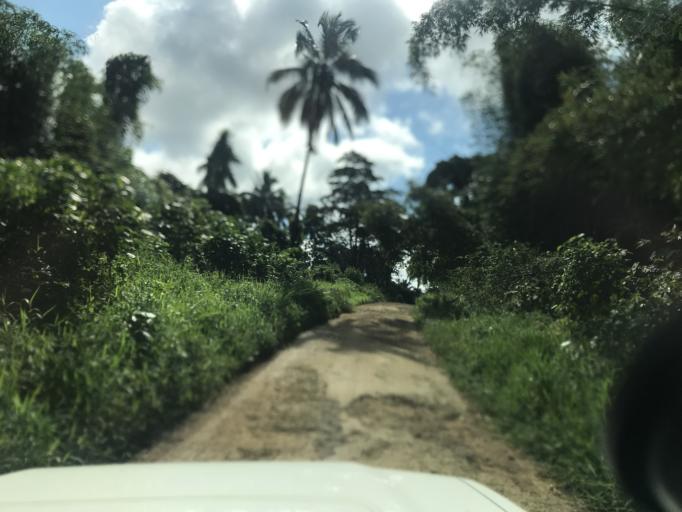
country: VU
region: Sanma
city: Luganville
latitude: -15.4647
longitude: 167.0717
